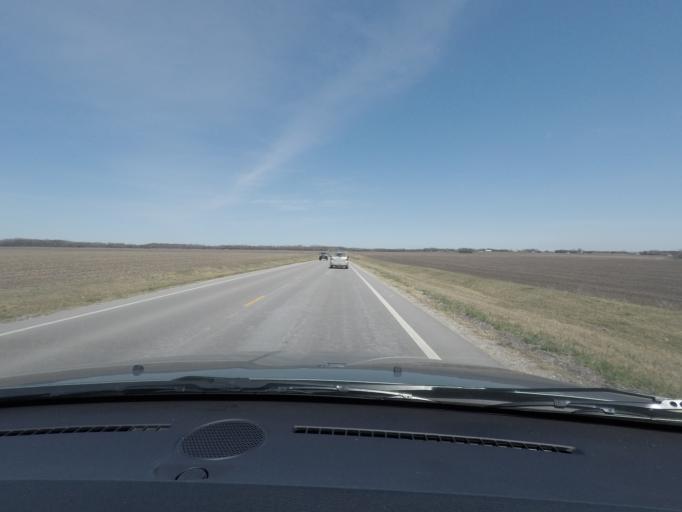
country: US
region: Kansas
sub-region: Lyon County
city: Emporia
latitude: 38.4375
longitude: -96.1705
